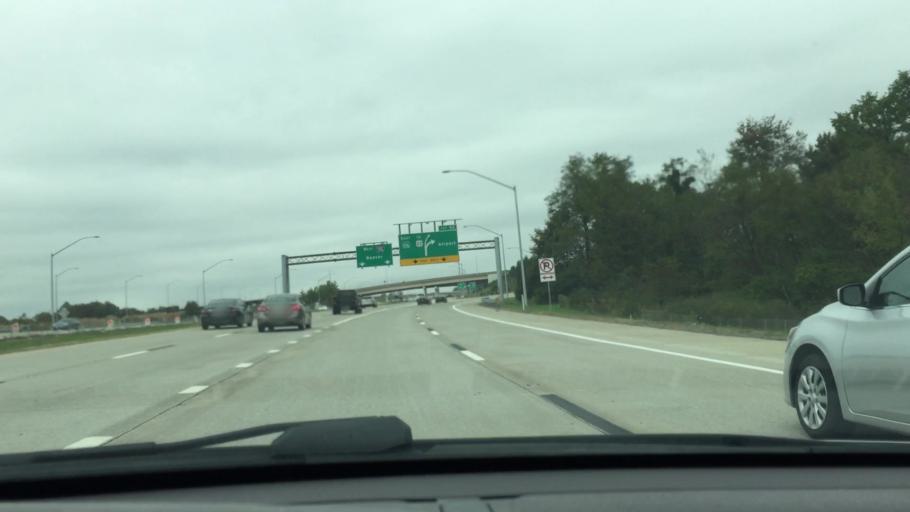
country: US
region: Pennsylvania
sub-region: Allegheny County
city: Imperial
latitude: 40.4833
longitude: -80.2625
